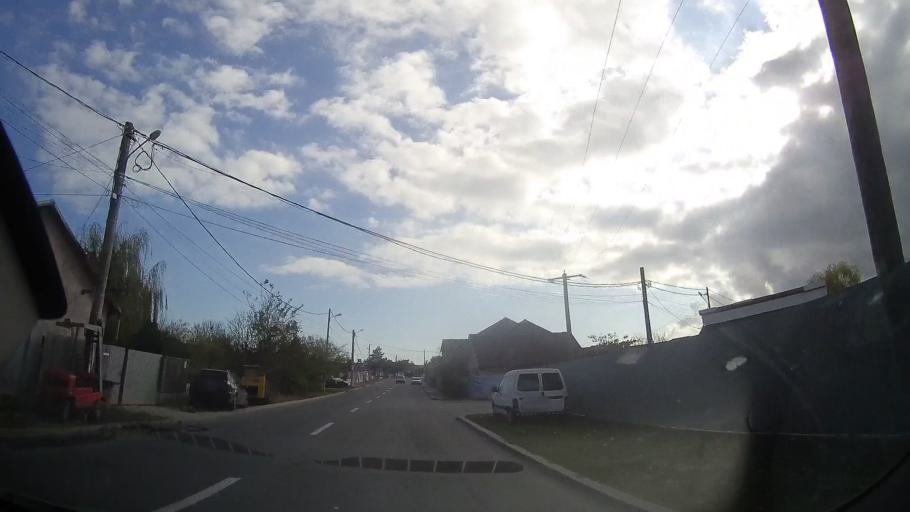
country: RO
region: Constanta
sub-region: Oras Techirghiol
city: Techirghiol
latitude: 44.0629
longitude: 28.5971
